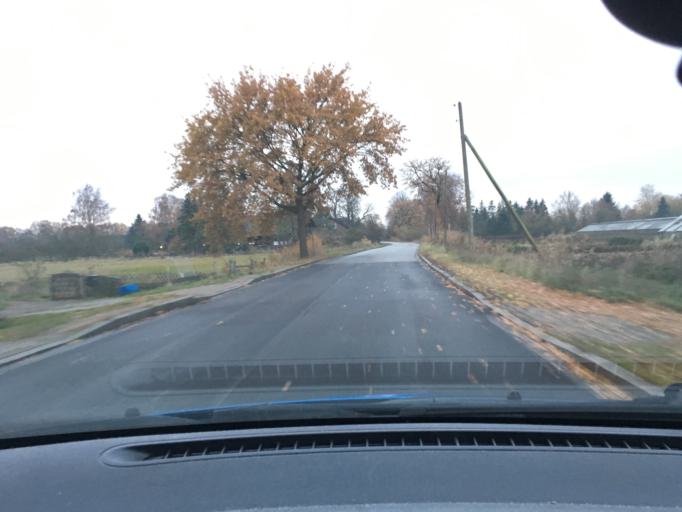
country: DE
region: Lower Saxony
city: Winsen
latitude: 53.4102
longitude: 10.2097
